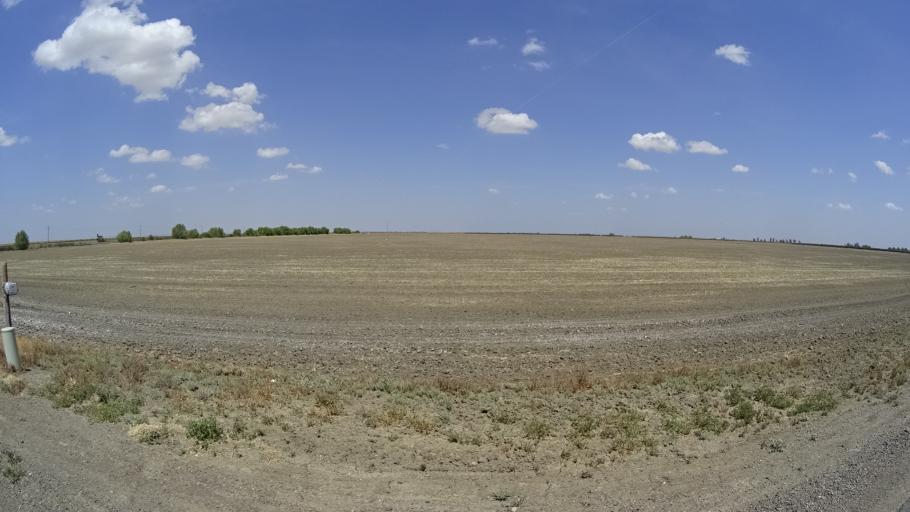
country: US
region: California
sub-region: Kings County
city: Stratford
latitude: 36.1895
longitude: -119.8702
